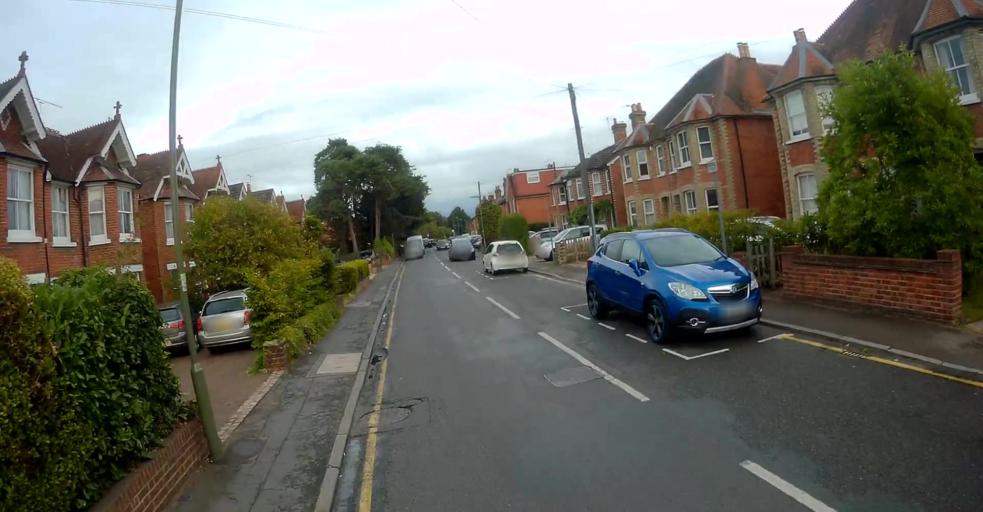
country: GB
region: England
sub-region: Surrey
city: Pirbright
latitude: 51.3044
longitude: -0.6433
